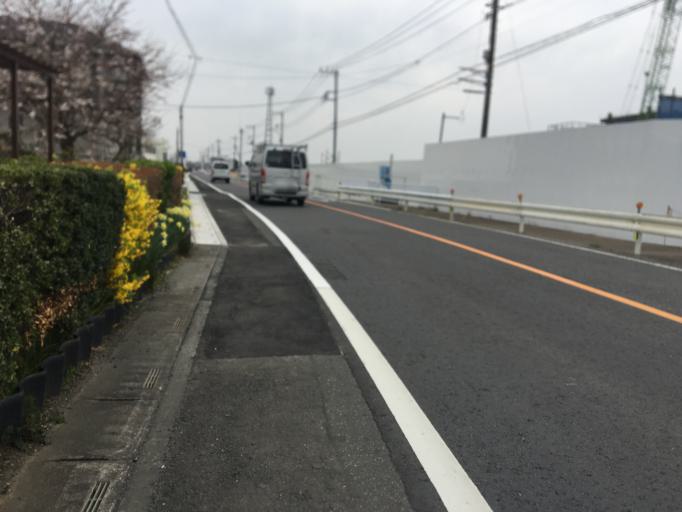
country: JP
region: Saitama
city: Kazo
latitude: 36.1182
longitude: 139.5966
